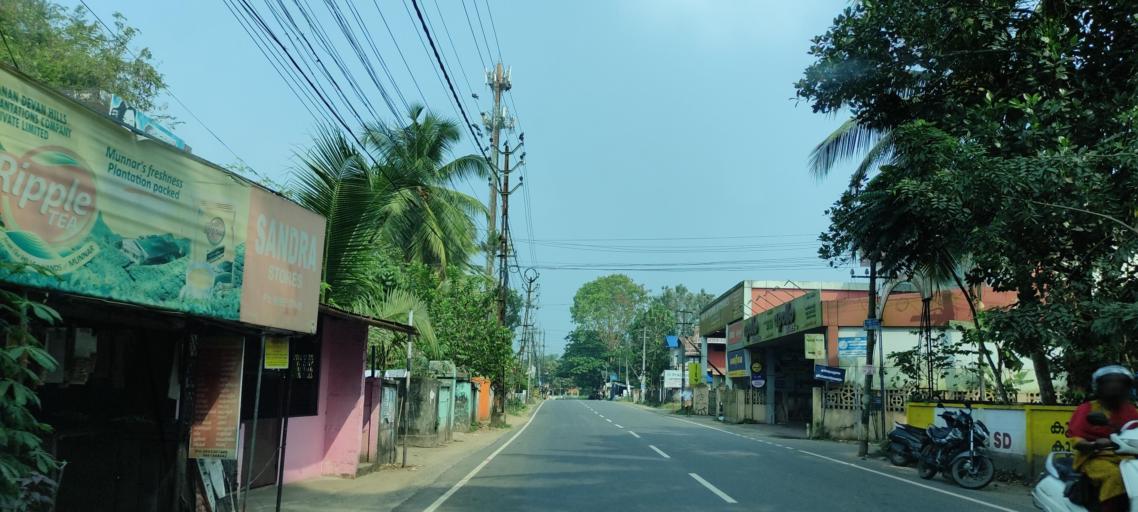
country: IN
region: Kerala
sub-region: Kottayam
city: Vaikam
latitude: 9.7585
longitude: 76.4062
